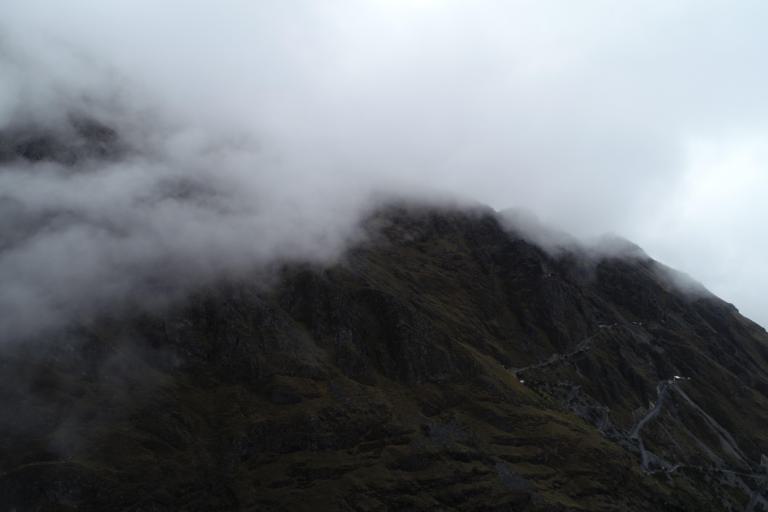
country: BO
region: La Paz
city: Sorata
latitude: -15.6610
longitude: -68.5359
